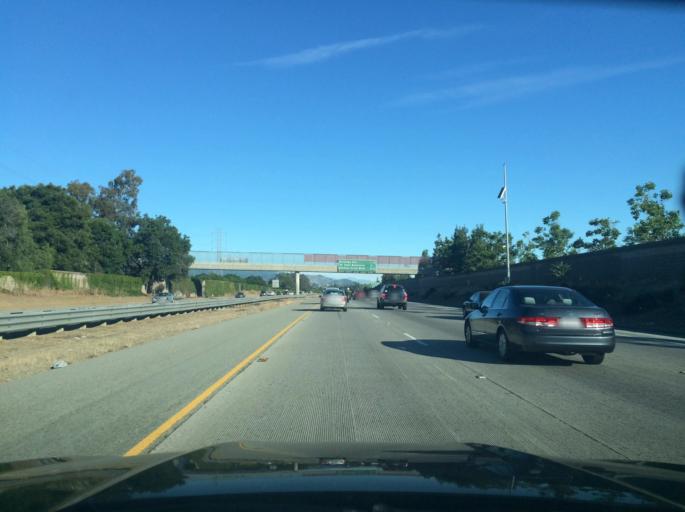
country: US
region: California
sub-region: Santa Clara County
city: Monte Sereno
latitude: 37.2673
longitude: -121.9854
